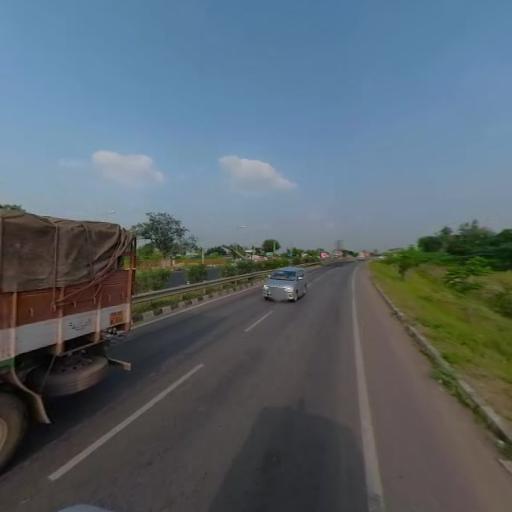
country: IN
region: Telangana
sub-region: Nalgonda
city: Suriapet
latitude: 17.1621
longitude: 79.5215
